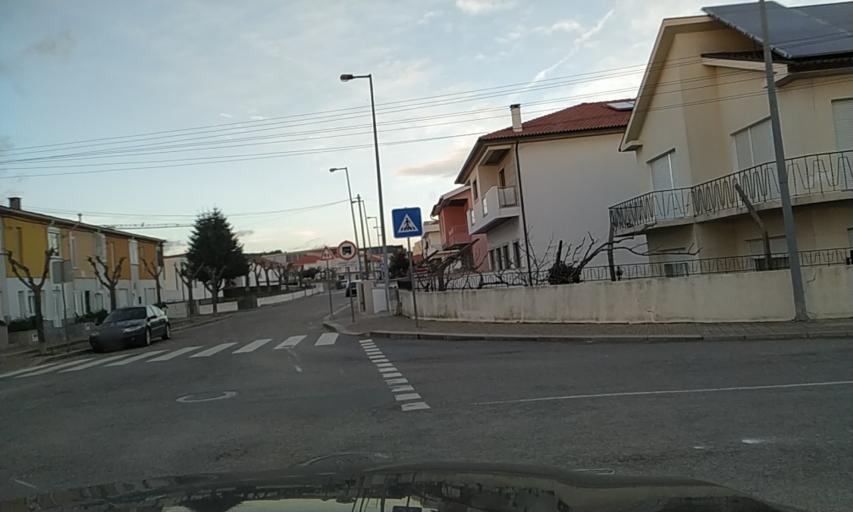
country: PT
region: Braganca
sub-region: Carrazeda de Ansiaes
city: Carrazeda de Anciaes
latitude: 41.2396
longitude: -7.3064
